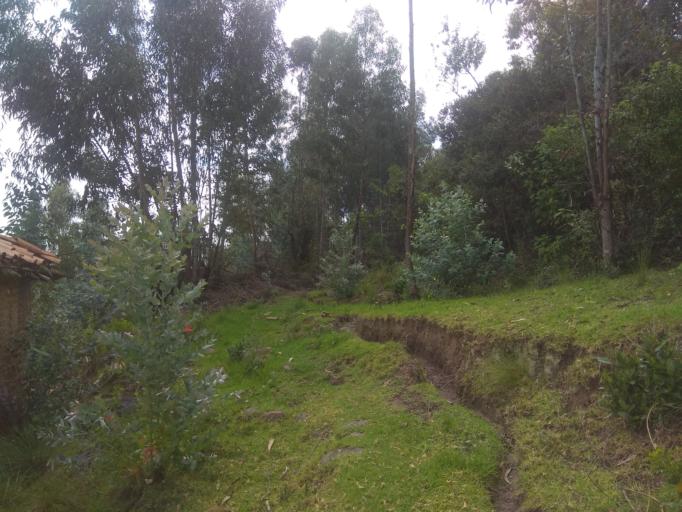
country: CO
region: Boyaca
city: Socha Viejo
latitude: 6.0097
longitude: -72.6747
